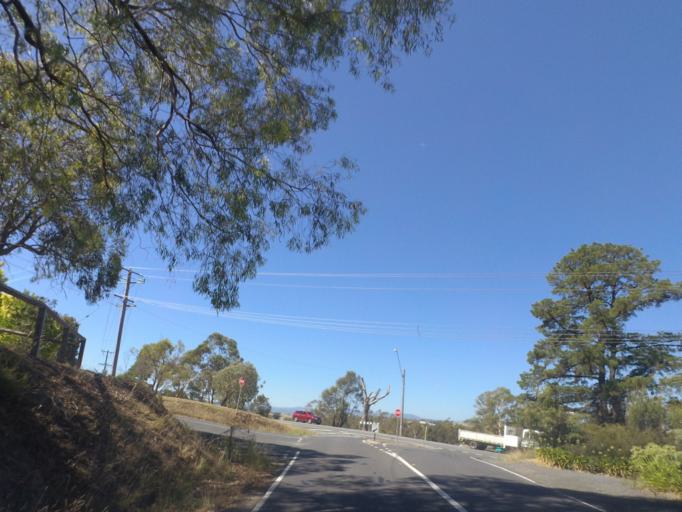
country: AU
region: Victoria
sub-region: Yarra Ranges
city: Chirnside Park
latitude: -37.7397
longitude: 145.2818
